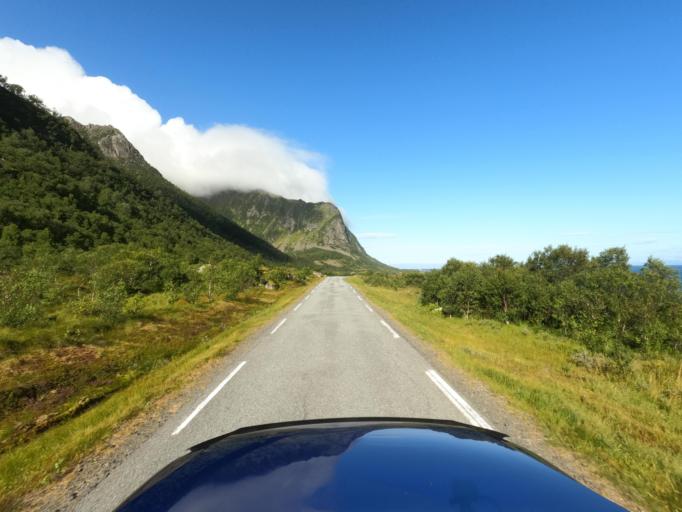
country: NO
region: Nordland
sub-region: Vagan
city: Kabelvag
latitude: 68.3010
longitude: 14.2635
